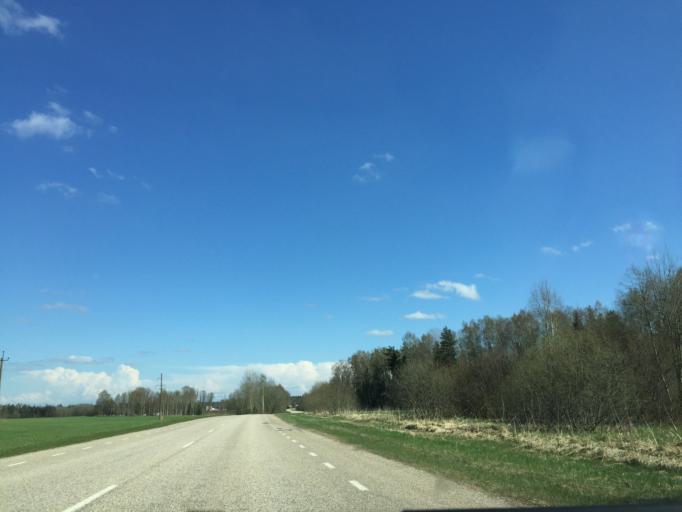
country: EE
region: Valgamaa
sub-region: Valga linn
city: Valga
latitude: 57.8702
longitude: 26.0794
